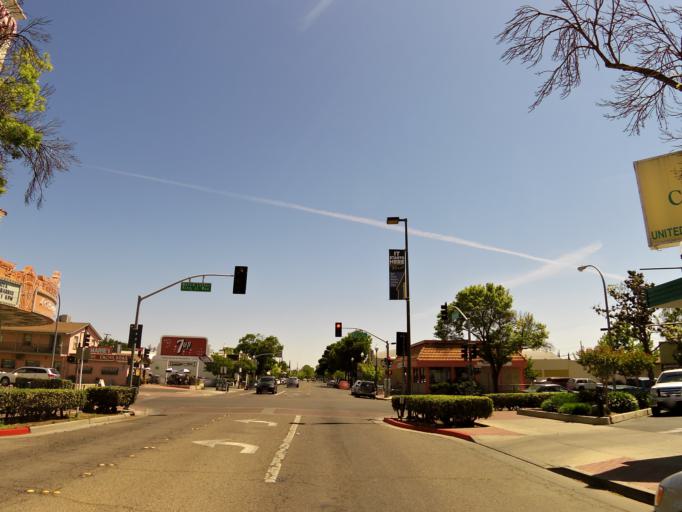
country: US
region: California
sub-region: Merced County
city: Merced
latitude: 37.3015
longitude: -120.4835
